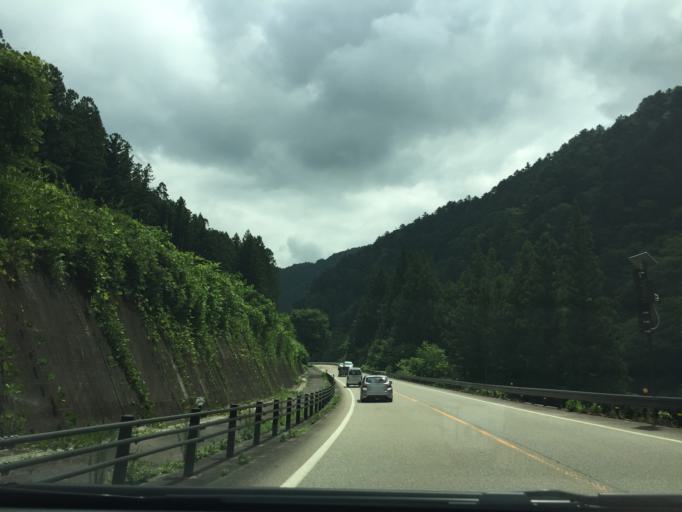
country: JP
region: Gifu
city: Gujo
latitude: 35.7782
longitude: 137.2430
